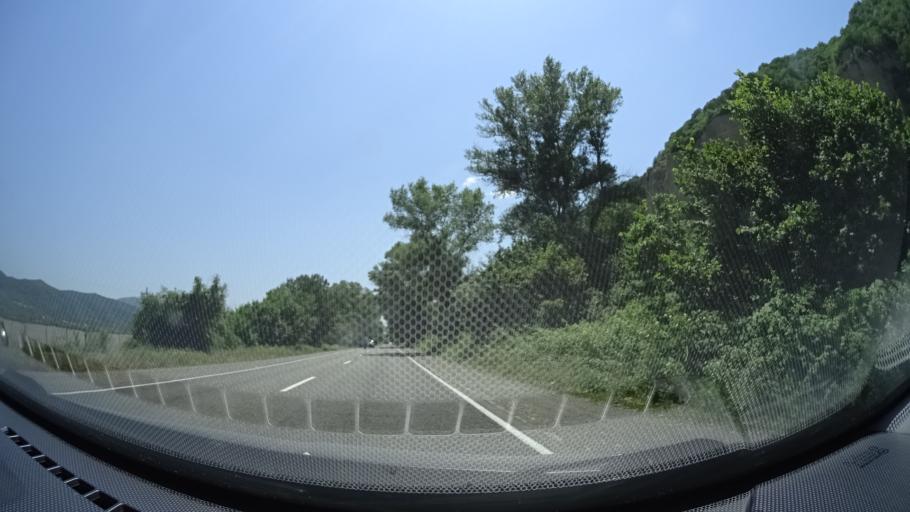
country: GE
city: Zhinvali
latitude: 42.0480
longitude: 44.7450
